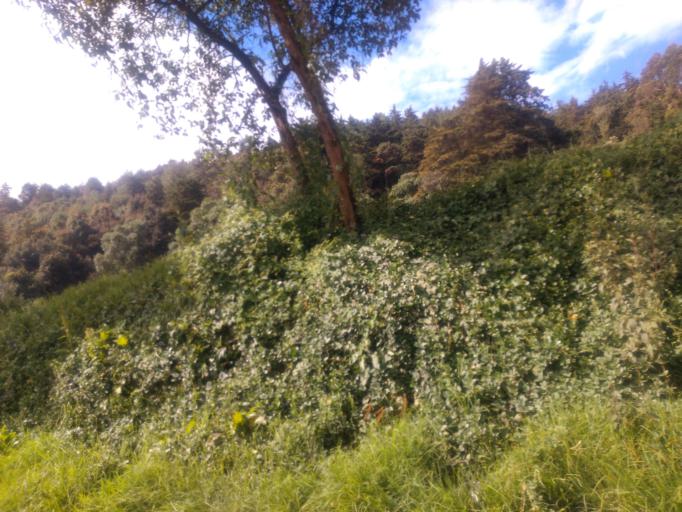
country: GT
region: Quetzaltenango
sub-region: Municipio de La Esperanza
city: La Esperanza
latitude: 14.8581
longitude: -91.5750
